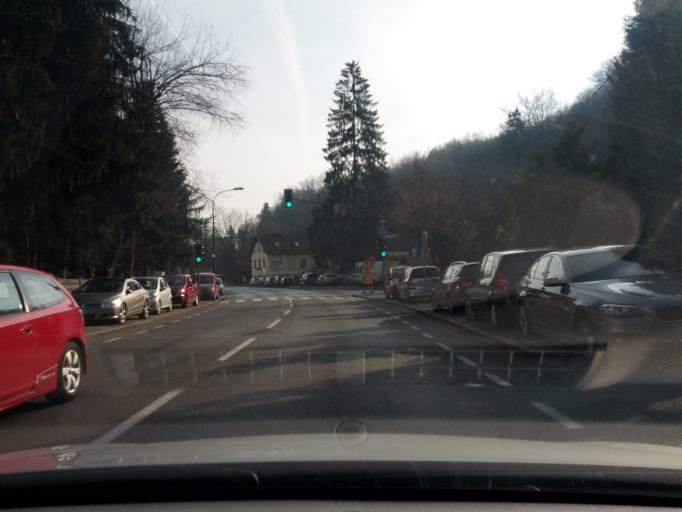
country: SI
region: Ljubljana
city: Ljubljana
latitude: 46.0674
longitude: 14.4862
